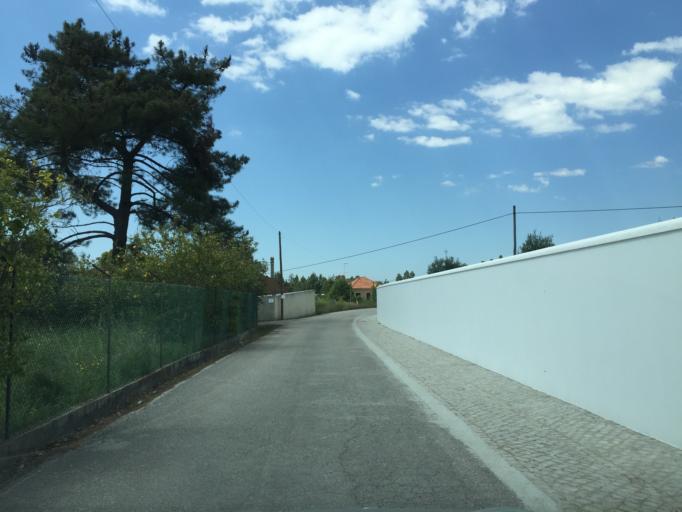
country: PT
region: Santarem
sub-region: Ourem
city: Ourem
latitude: 39.6796
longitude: -8.5663
